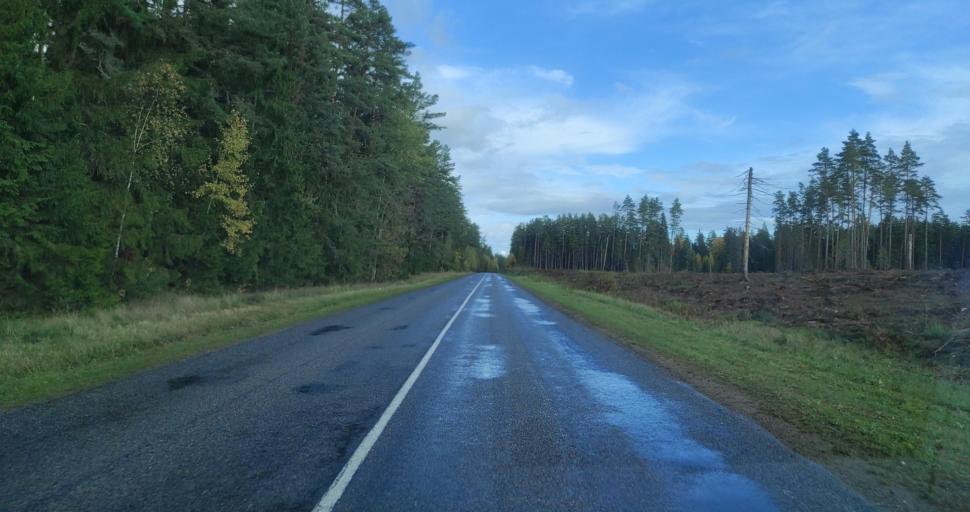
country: LV
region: Skrunda
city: Skrunda
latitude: 56.6367
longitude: 22.0060
